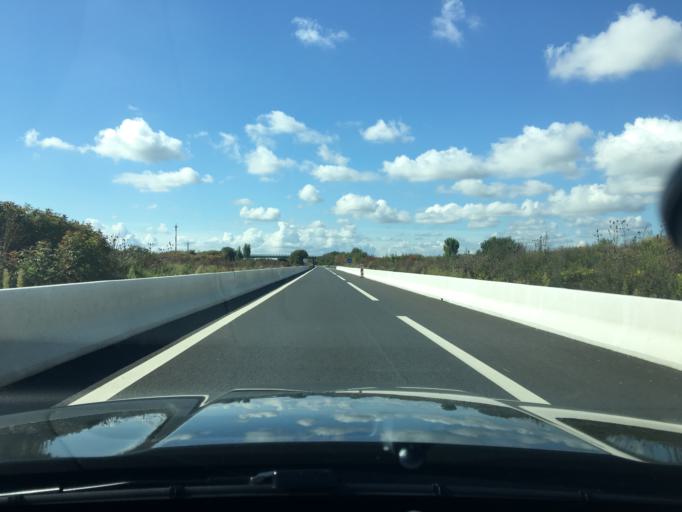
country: FR
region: Ile-de-France
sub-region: Departement du Val-d'Oise
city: Roissy-en-France
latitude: 49.0291
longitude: 2.5369
